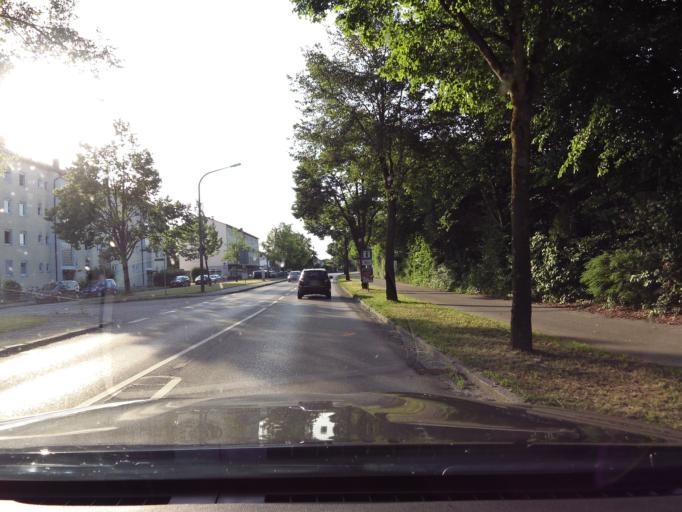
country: DE
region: Bavaria
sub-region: Upper Bavaria
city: Burgkirchen an der Alz
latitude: 48.1622
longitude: 12.7391
